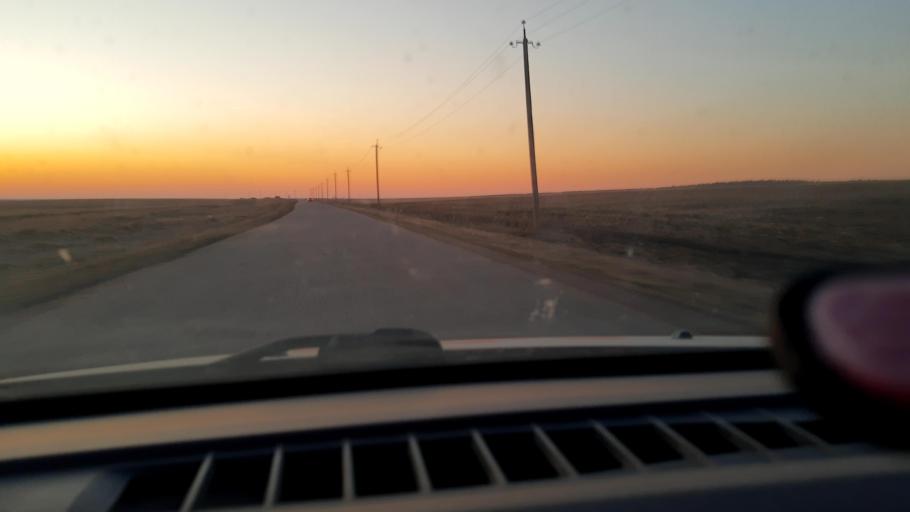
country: RU
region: Bashkortostan
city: Asanovo
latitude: 54.8025
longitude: 55.4919
